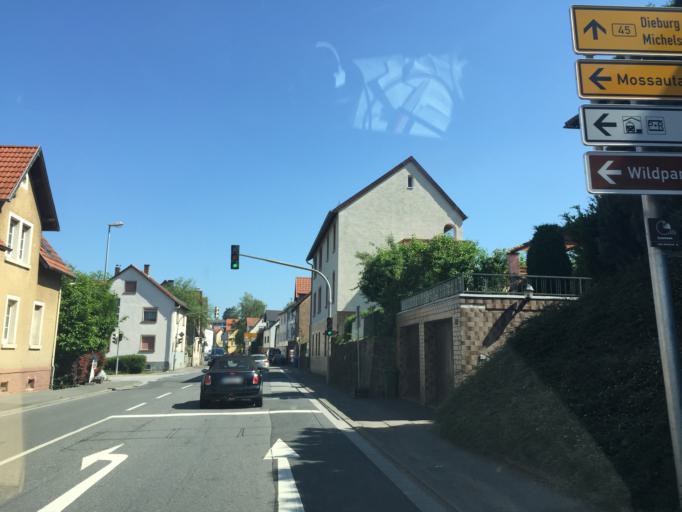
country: DE
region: Hesse
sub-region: Regierungsbezirk Darmstadt
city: Erbach
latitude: 49.6532
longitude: 8.9953
